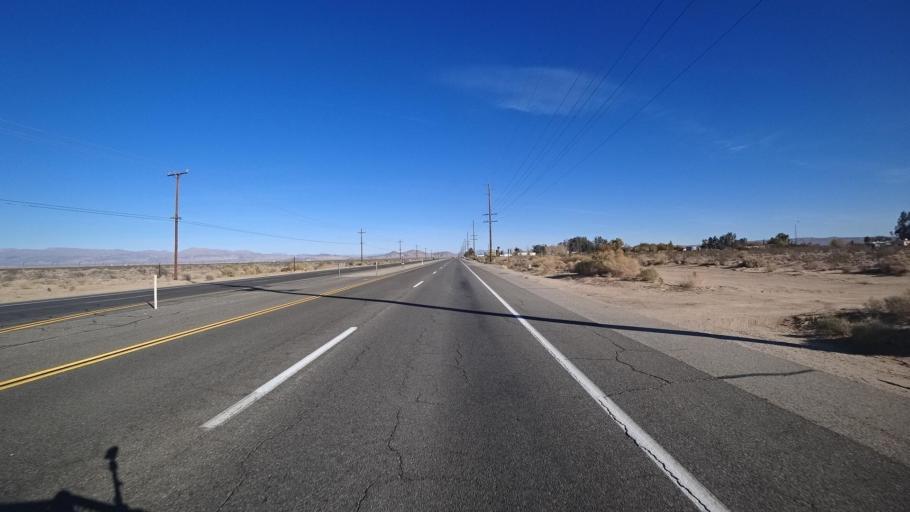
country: US
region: California
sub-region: Kern County
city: China Lake Acres
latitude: 35.6515
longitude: -117.7526
